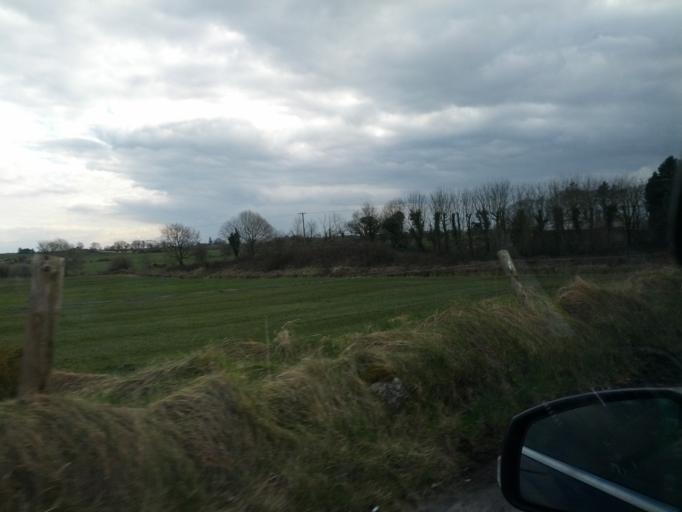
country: IE
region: Connaught
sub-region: County Galway
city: Athenry
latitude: 53.4953
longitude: -8.6062
